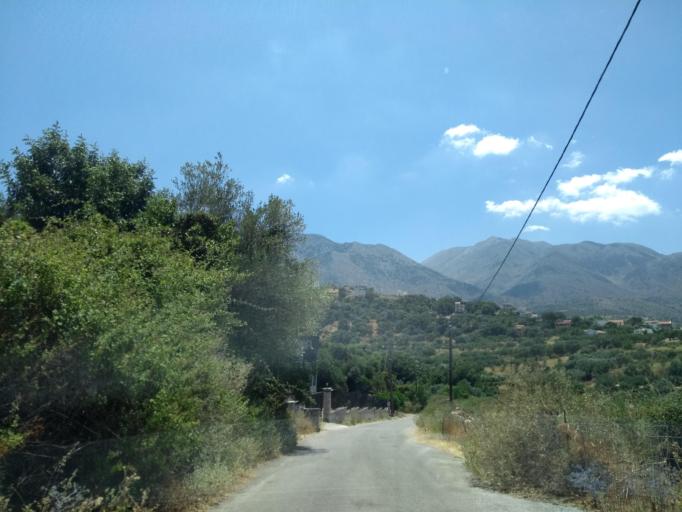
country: GR
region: Crete
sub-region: Nomos Chanias
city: Georgioupolis
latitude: 35.3183
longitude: 24.3144
